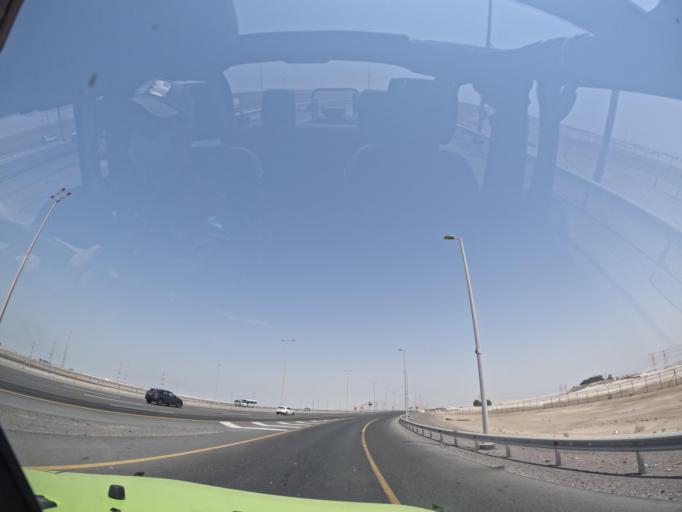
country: AE
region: Abu Dhabi
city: Abu Dhabi
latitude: 24.2136
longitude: 54.4168
